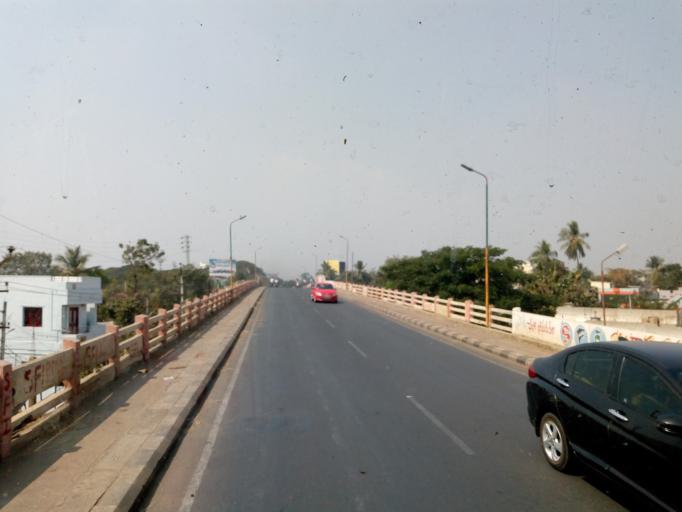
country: IN
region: Andhra Pradesh
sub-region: West Godavari
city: Eluru
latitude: 16.7088
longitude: 81.0989
